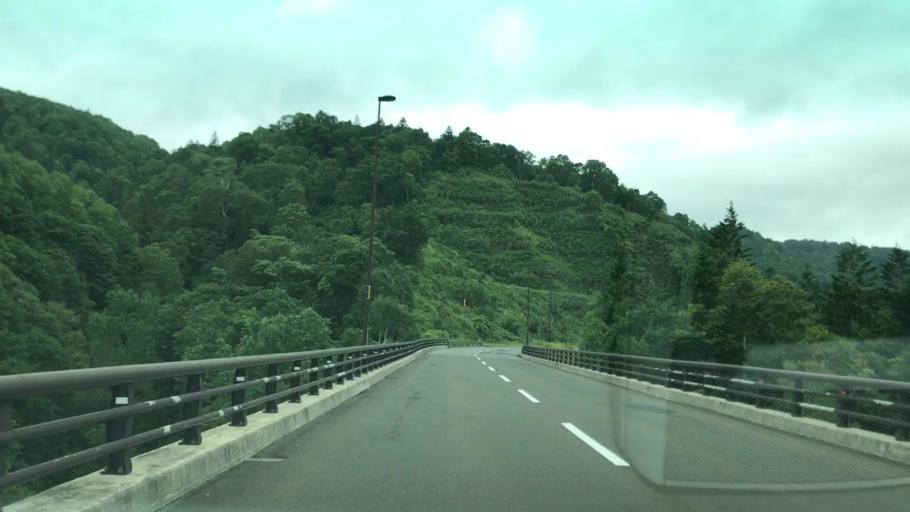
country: JP
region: Hokkaido
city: Otaru
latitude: 42.9922
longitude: 140.8763
